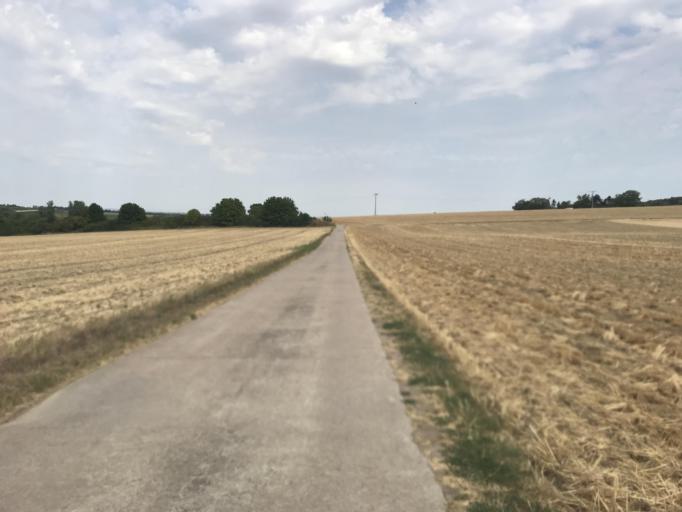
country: DE
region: Rheinland-Pfalz
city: Sorgenloch
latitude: 49.8701
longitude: 8.1985
